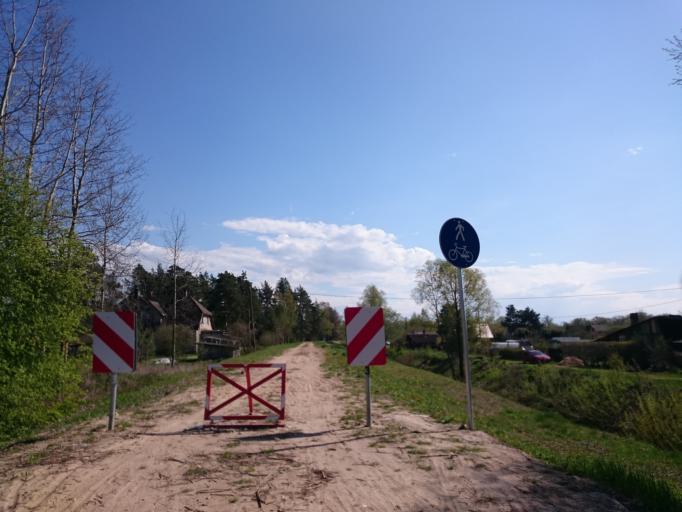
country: LV
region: Adazi
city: Adazi
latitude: 57.0988
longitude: 24.3288
